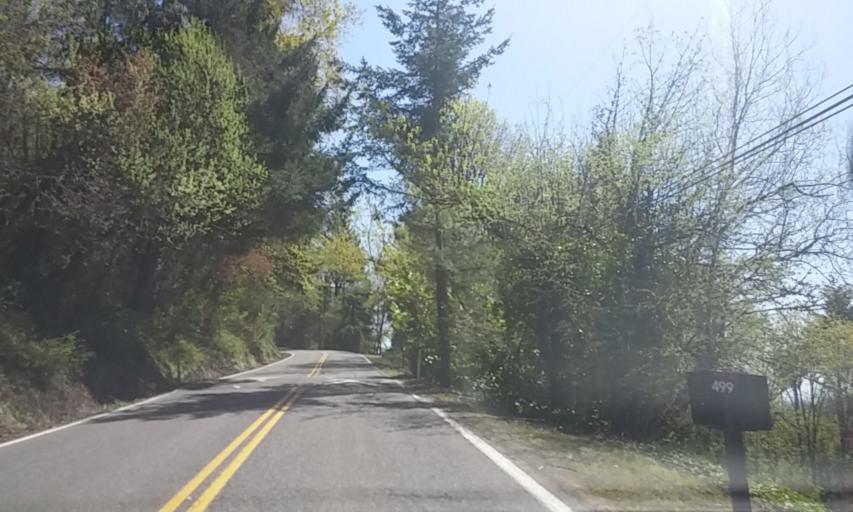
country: US
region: Oregon
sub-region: Washington County
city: West Haven-Sylvan
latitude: 45.5267
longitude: -122.7567
